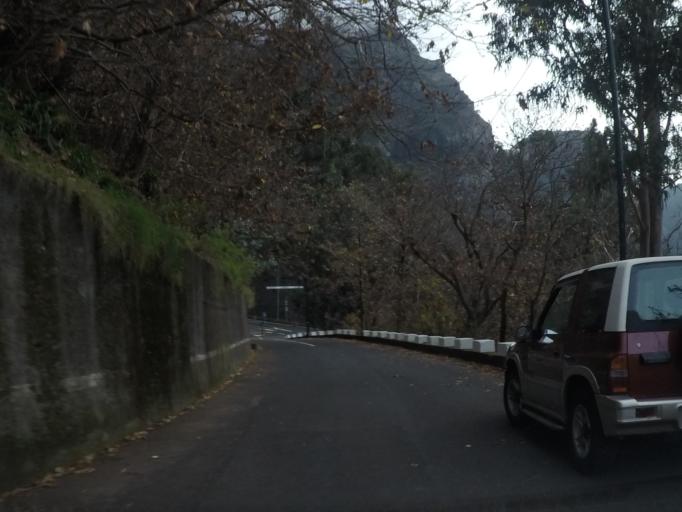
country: PT
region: Madeira
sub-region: Camara de Lobos
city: Curral das Freiras
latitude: 32.7249
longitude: -16.9623
